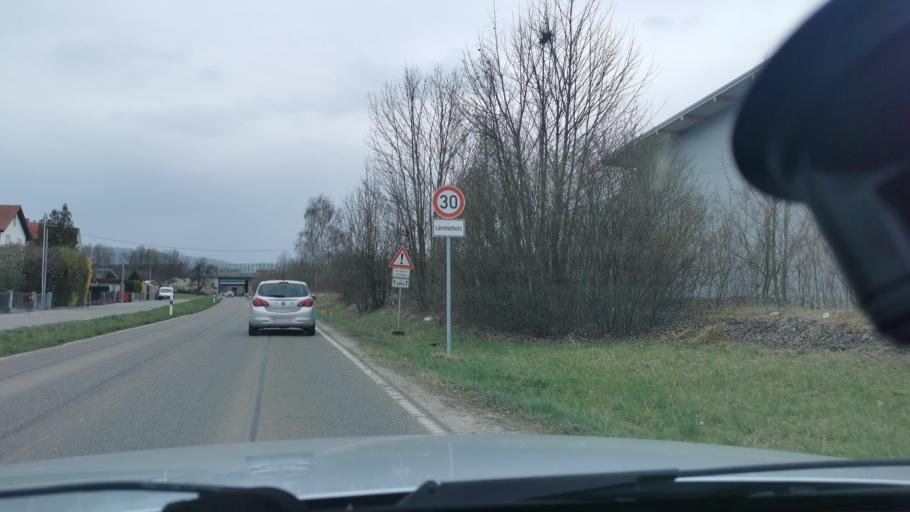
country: DE
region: Baden-Wuerttemberg
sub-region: Regierungsbezirk Stuttgart
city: Holzmaden
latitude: 48.6301
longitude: 9.5140
